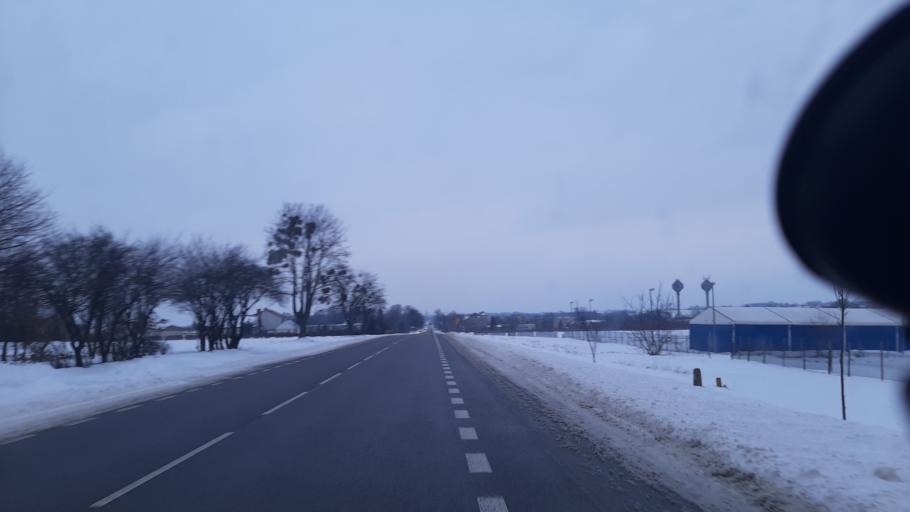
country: PL
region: Lublin Voivodeship
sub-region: Powiat pulawski
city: Markuszow
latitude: 51.3673
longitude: 22.2877
